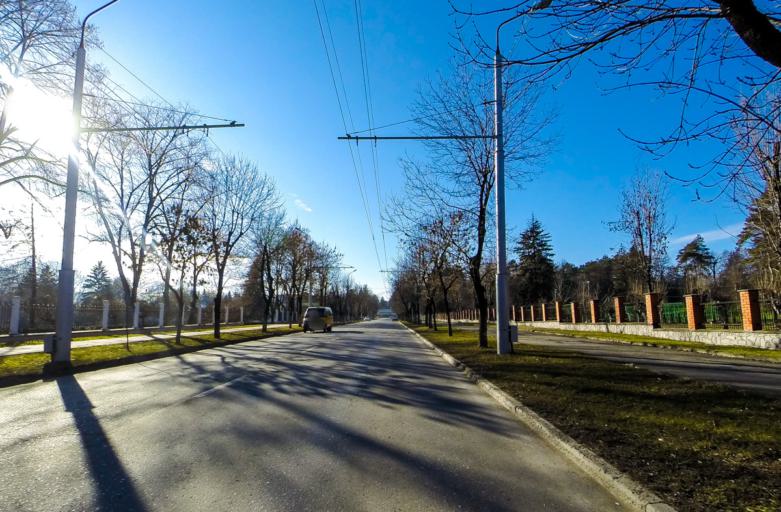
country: RU
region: Kabardino-Balkariya
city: Vol'nyy Aul
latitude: 43.4563
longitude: 43.5831
